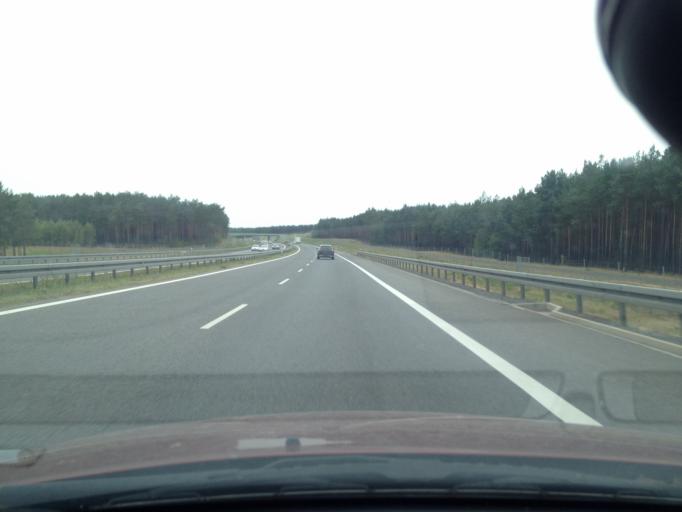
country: PL
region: Lubusz
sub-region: Powiat miedzyrzecki
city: Skwierzyna
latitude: 52.6068
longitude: 15.4193
